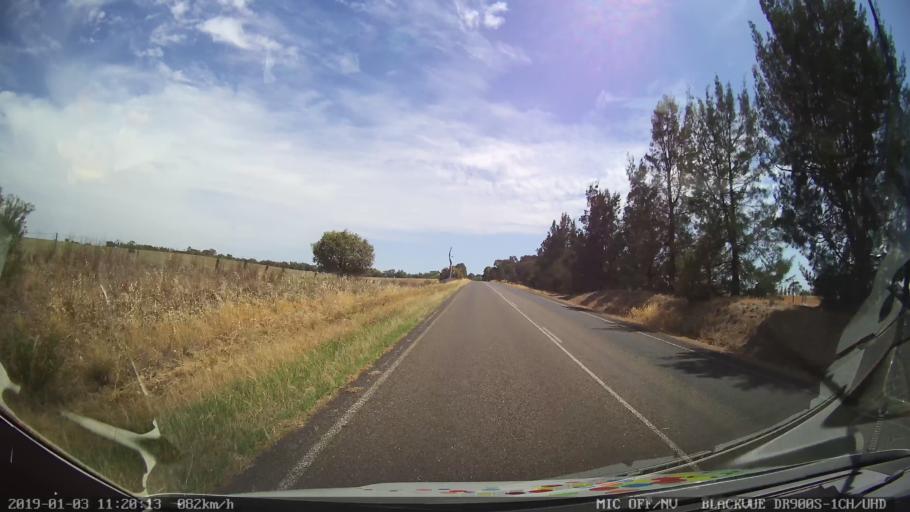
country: AU
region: New South Wales
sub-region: Young
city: Young
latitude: -34.1038
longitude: 148.2551
